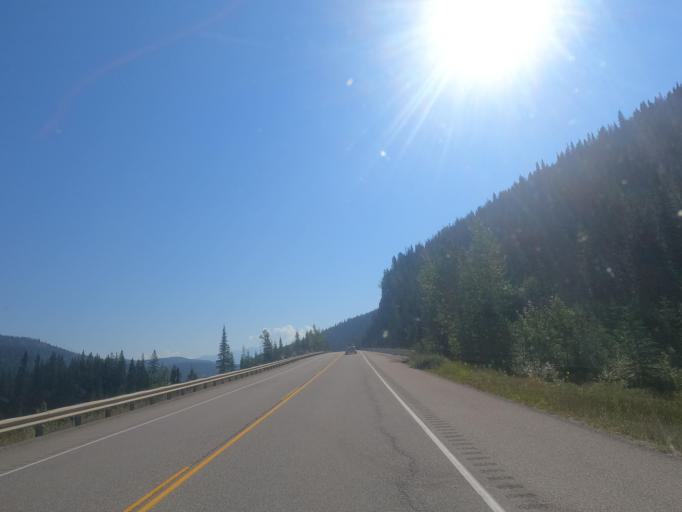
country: CA
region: Alberta
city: Jasper Park Lodge
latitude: 52.8747
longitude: -118.3109
